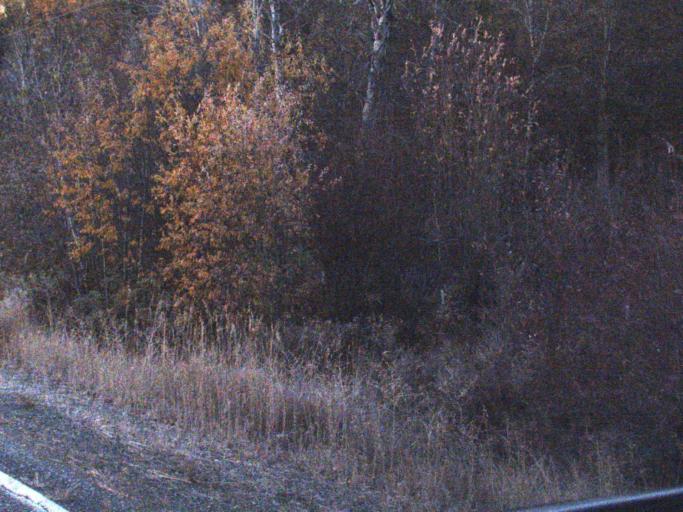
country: US
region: Washington
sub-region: Ferry County
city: Republic
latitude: 48.4518
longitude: -118.7466
